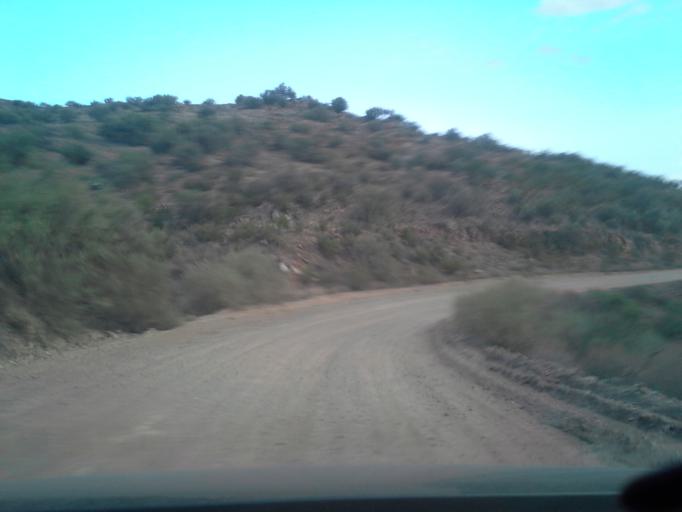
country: US
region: Arizona
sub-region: Yavapai County
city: Black Canyon City
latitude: 34.1782
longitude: -112.1644
